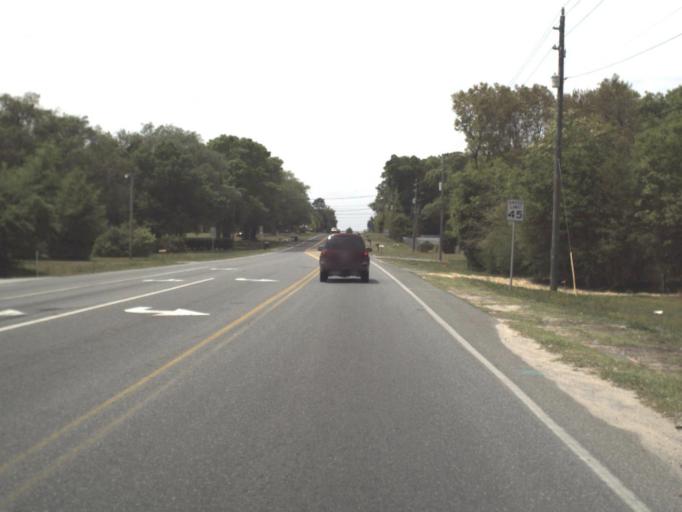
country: US
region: Florida
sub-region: Escambia County
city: Bellview
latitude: 30.4868
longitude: -87.3069
